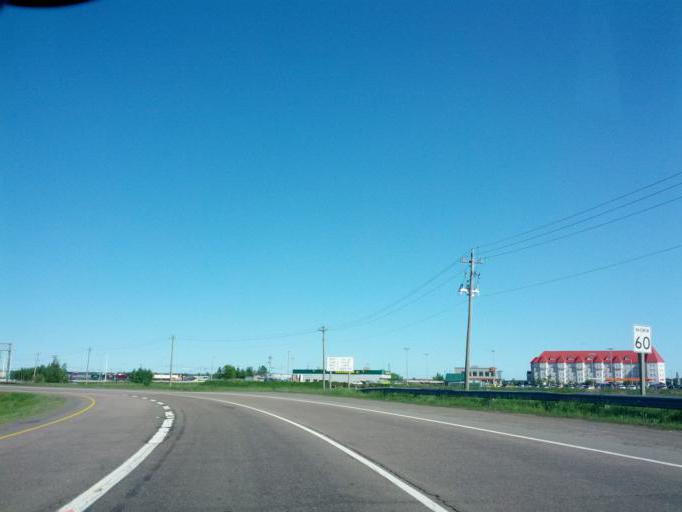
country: CA
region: New Brunswick
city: Moncton
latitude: 46.0962
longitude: -64.7687
